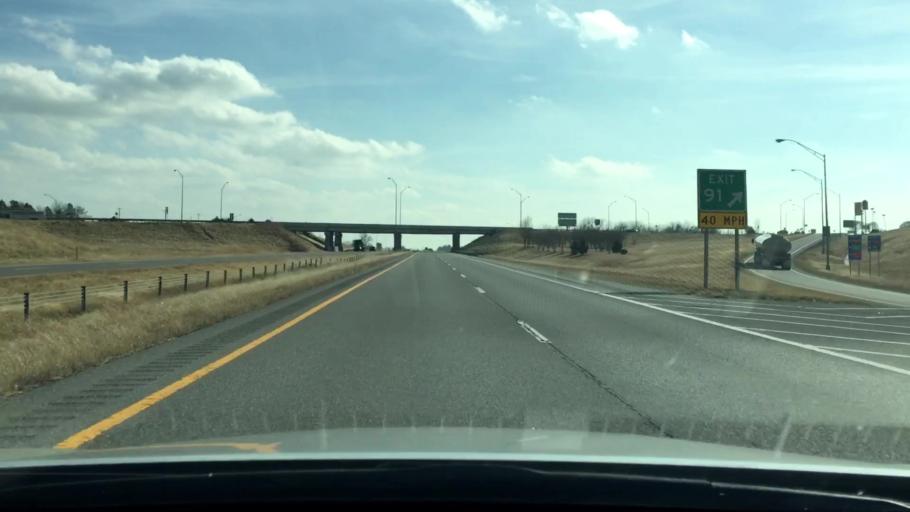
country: US
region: Oklahoma
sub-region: McClain County
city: Purcell
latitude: 34.9849
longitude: -97.3731
